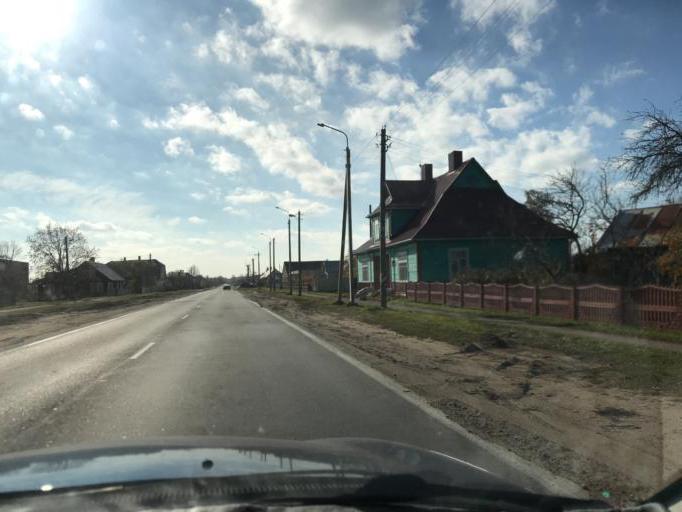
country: LT
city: Salcininkai
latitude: 54.2551
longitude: 25.3567
